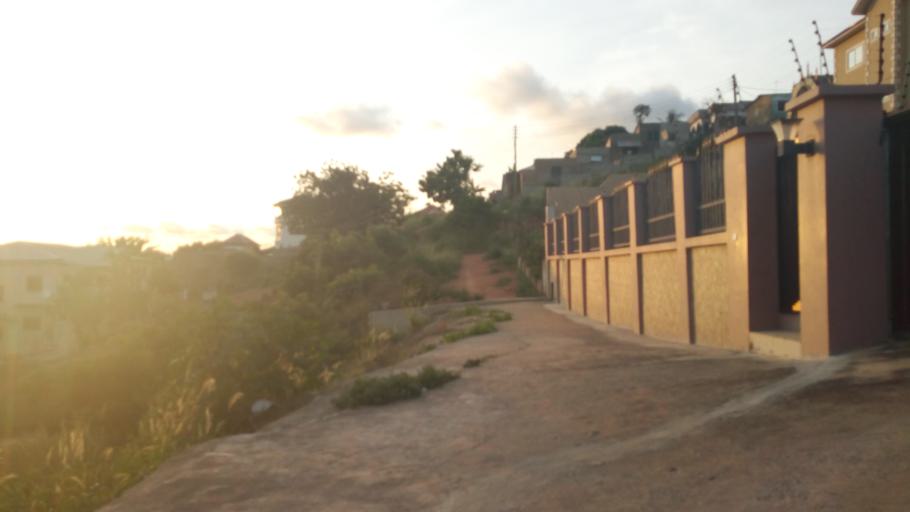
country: GH
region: Greater Accra
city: Gbawe
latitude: 5.5608
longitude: -0.3060
